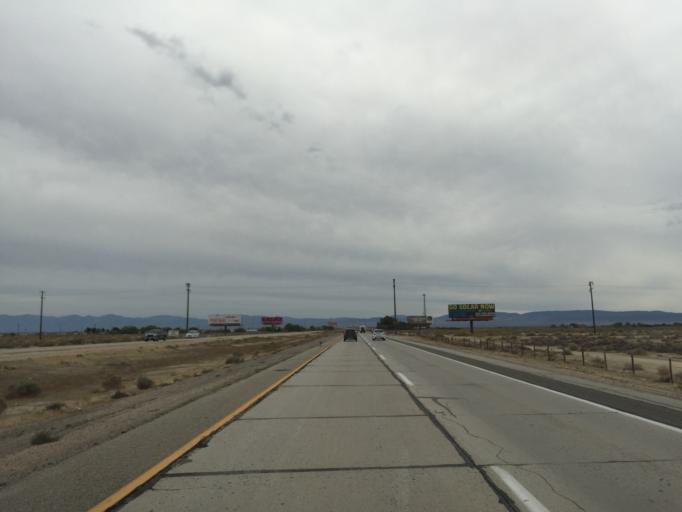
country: US
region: California
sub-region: Kern County
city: Rosamond
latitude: 34.8366
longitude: -118.1708
